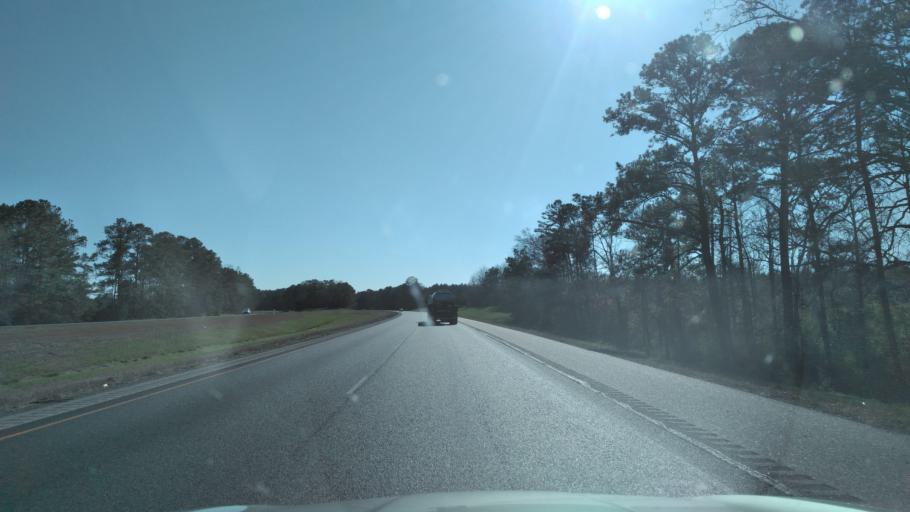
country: US
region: Alabama
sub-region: Butler County
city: Greenville
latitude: 31.7698
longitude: -86.6962
